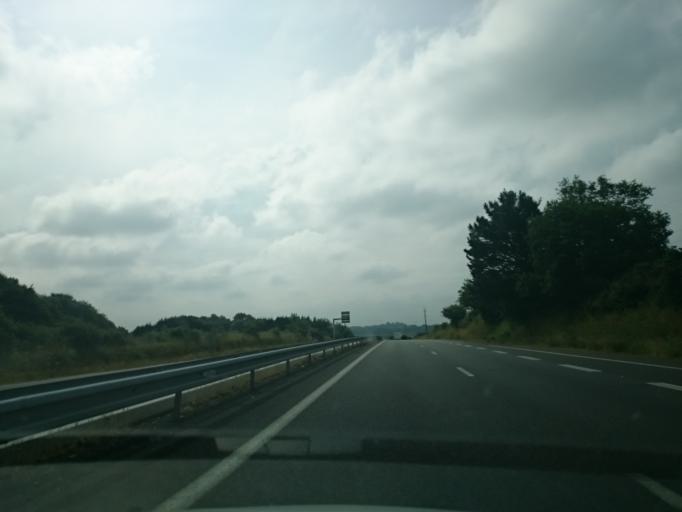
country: FR
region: Brittany
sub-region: Departement du Morbihan
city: Muzillac
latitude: 47.5569
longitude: -2.4977
